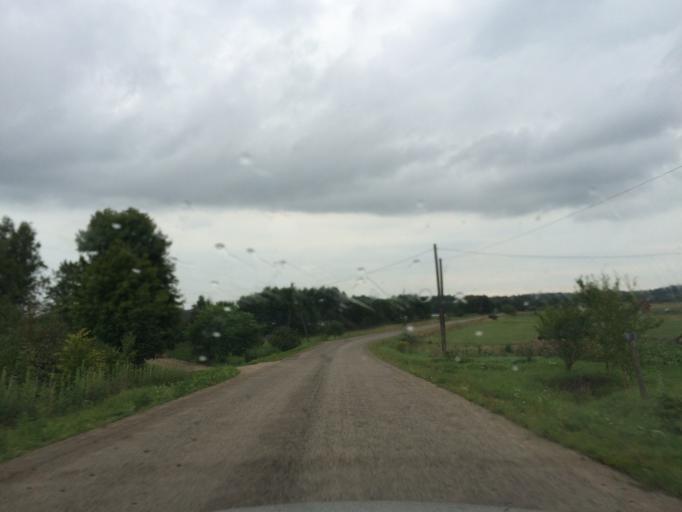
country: LV
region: Rezekne
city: Rezekne
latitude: 56.5538
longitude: 27.4010
